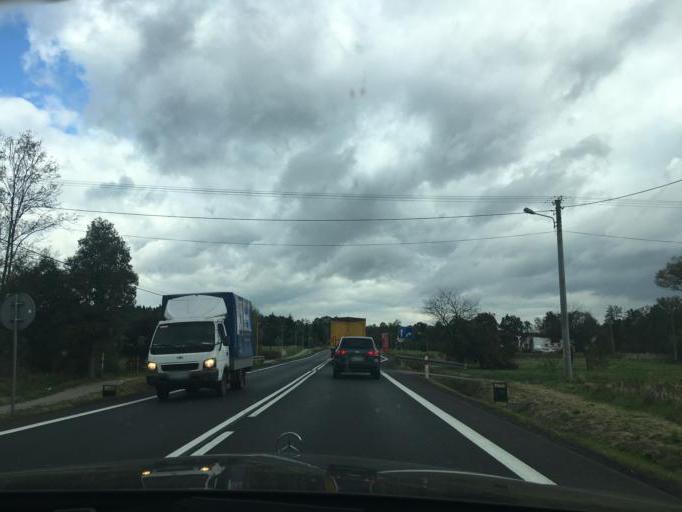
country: PL
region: Subcarpathian Voivodeship
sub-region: Powiat strzyzowski
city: Babica
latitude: 49.9107
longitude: 21.8666
